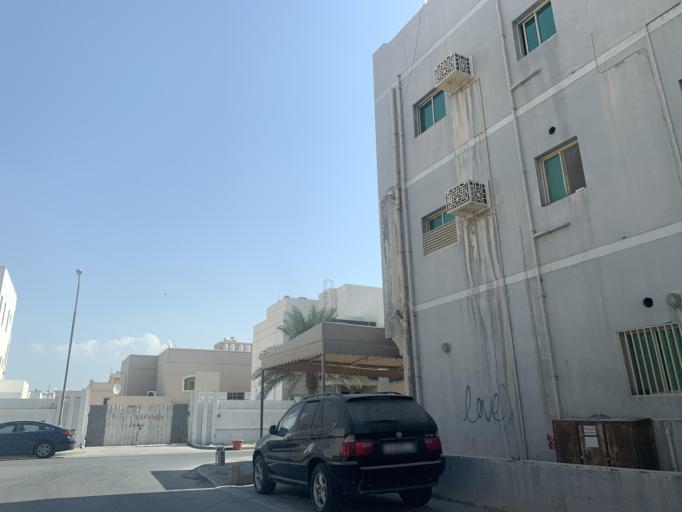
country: BH
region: Central Governorate
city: Madinat Hamad
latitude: 26.1368
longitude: 50.4929
